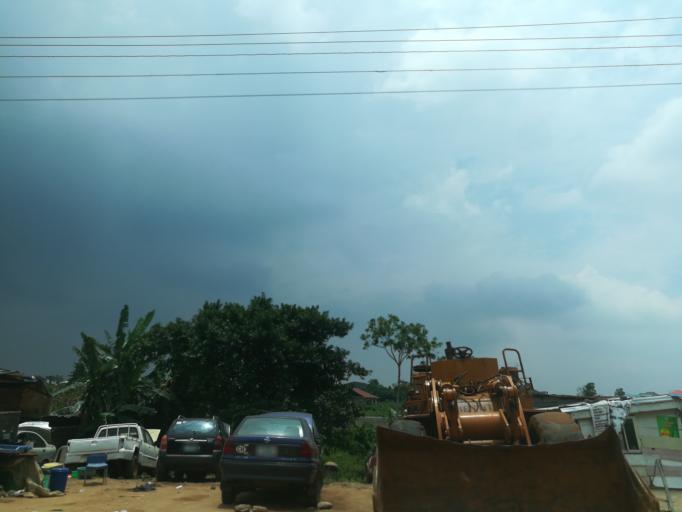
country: NG
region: Lagos
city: Ikorodu
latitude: 6.6107
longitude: 3.5810
